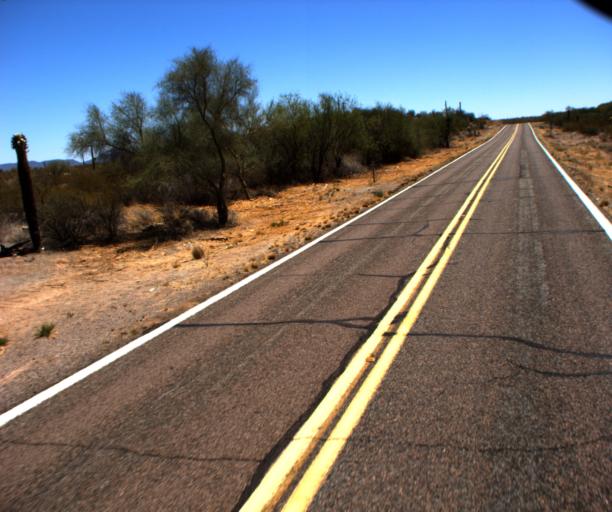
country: US
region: Arizona
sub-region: Pima County
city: Ajo
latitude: 32.2229
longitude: -112.6828
